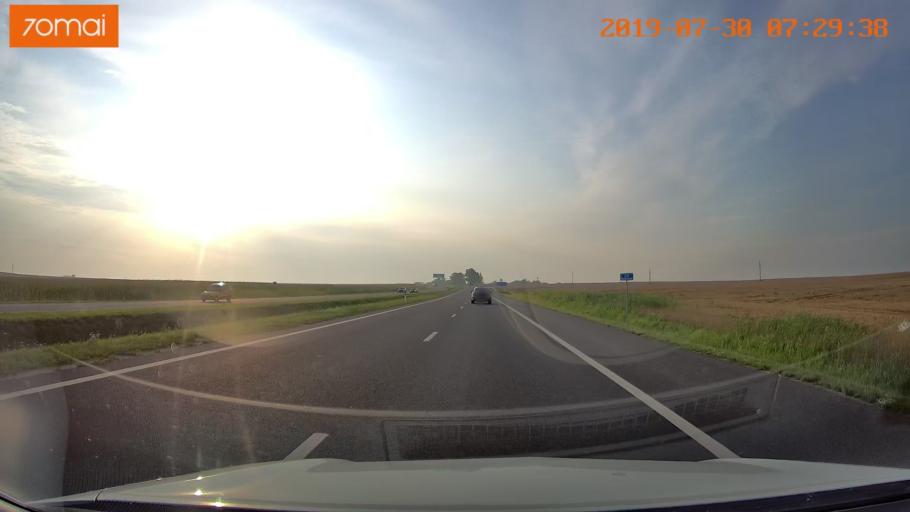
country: RU
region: Kaliningrad
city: Gvardeysk
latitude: 54.6712
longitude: 20.9445
